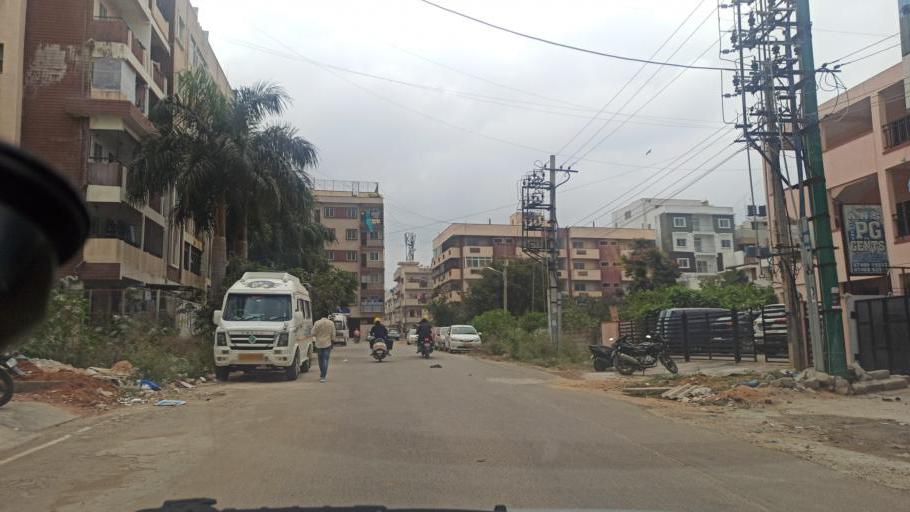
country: IN
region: Karnataka
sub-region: Bangalore Urban
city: Yelahanka
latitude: 13.0372
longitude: 77.6171
